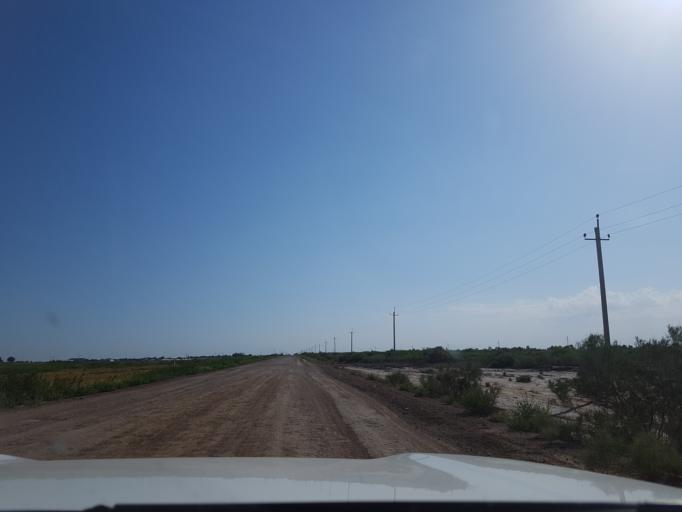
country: TM
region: Dasoguz
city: Koeneuergench
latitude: 42.0589
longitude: 58.8426
